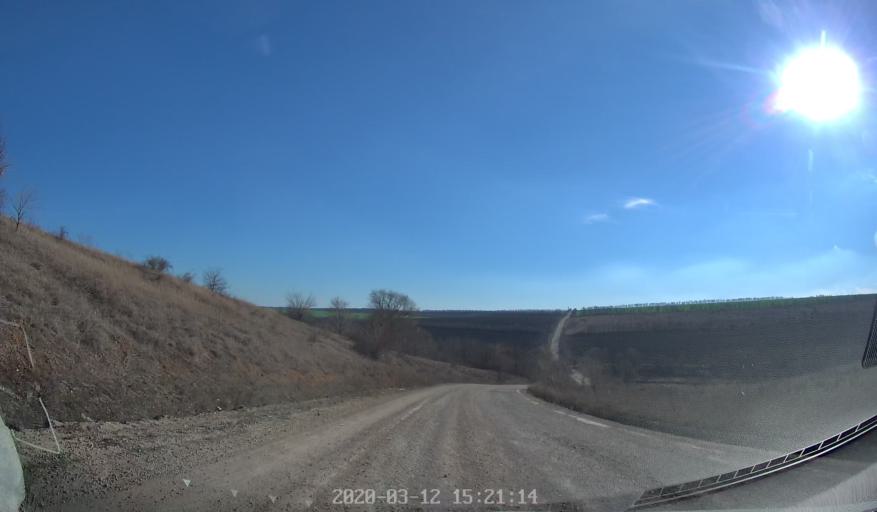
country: MD
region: Chisinau
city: Ciorescu
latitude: 47.2037
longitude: 28.9229
